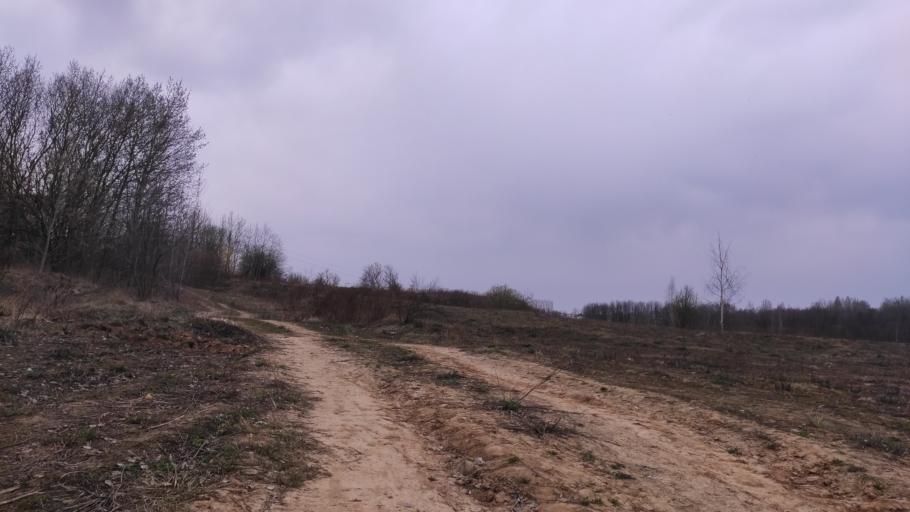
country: BY
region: Minsk
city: Novoye Medvezhino
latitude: 53.8836
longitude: 27.4666
